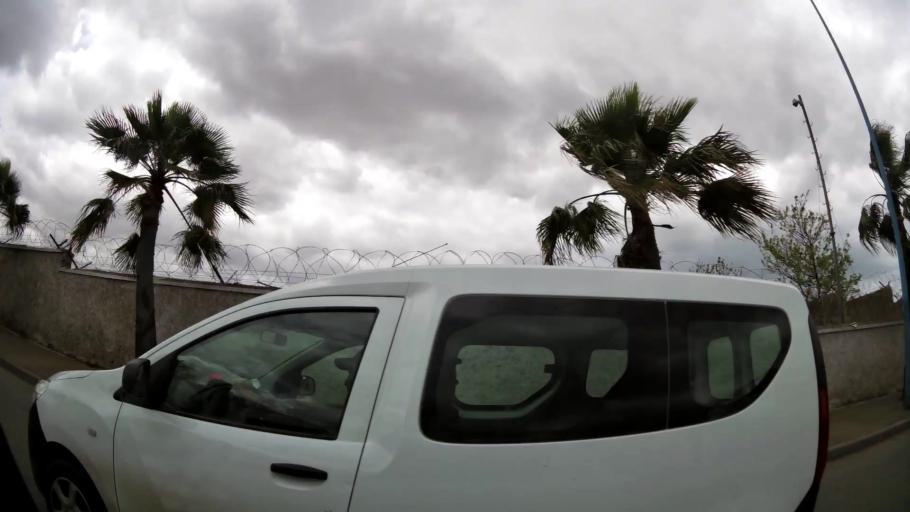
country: MA
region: Grand Casablanca
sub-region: Casablanca
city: Casablanca
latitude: 33.5942
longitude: -7.5457
